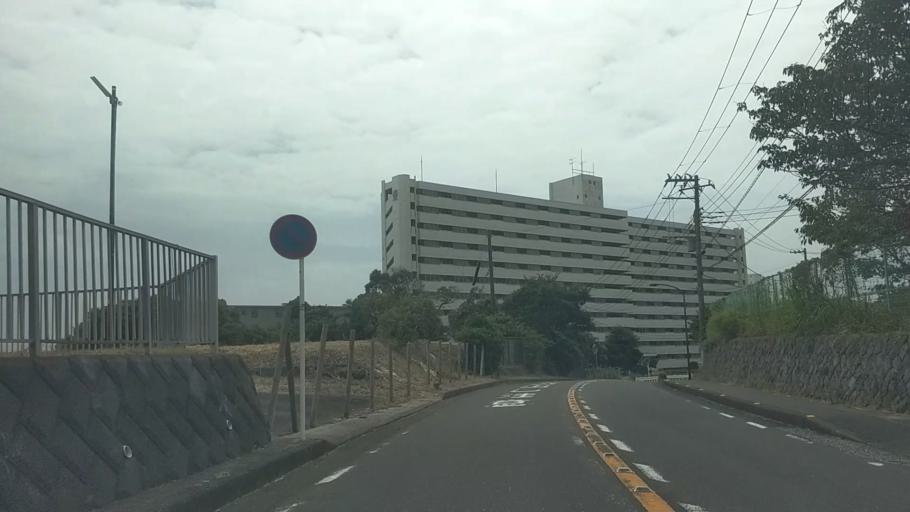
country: JP
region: Kanagawa
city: Yokosuka
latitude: 35.2440
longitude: 139.7335
